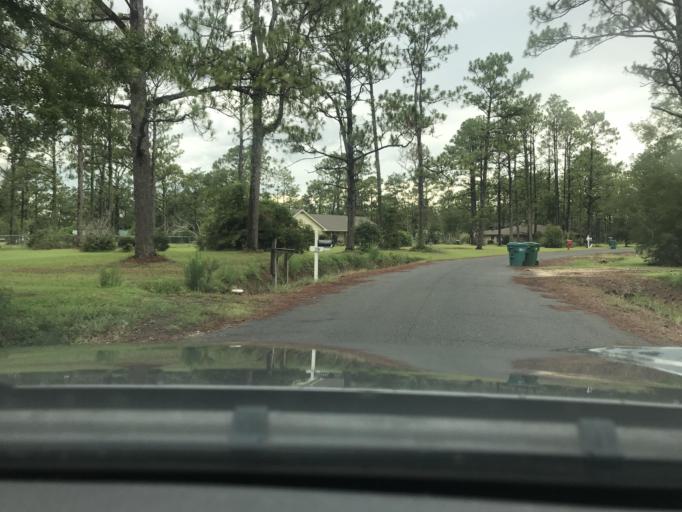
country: US
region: Louisiana
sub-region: Calcasieu Parish
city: Moss Bluff
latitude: 30.3381
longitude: -93.2610
